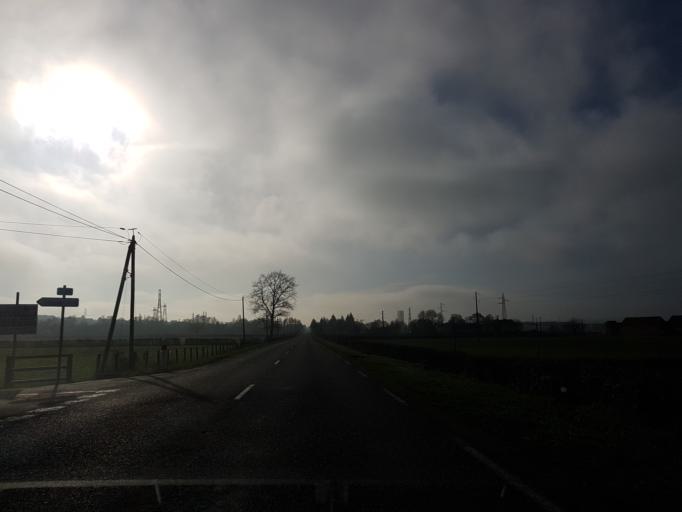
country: FR
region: Bourgogne
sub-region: Departement de Saone-et-Loire
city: Gueugnon
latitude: 46.6158
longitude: 4.0789
